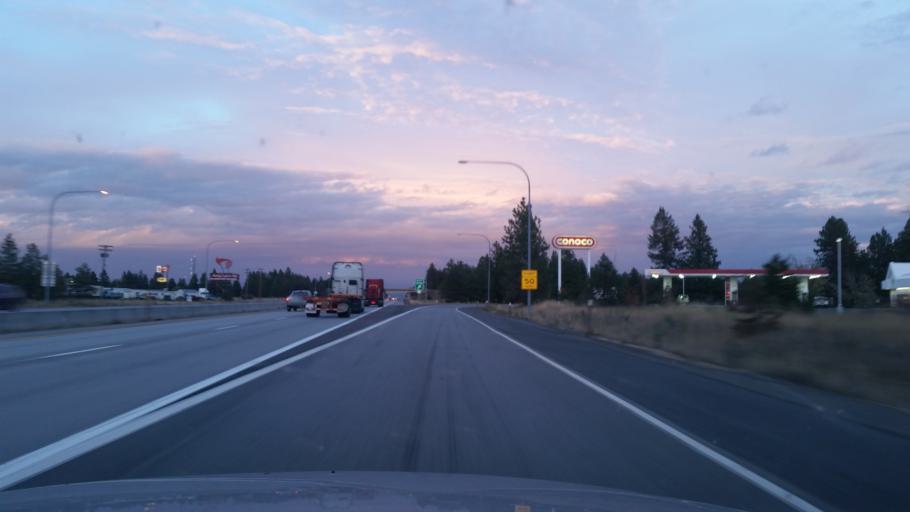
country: US
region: Washington
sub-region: Spokane County
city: Spokane
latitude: 47.6169
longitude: -117.5078
